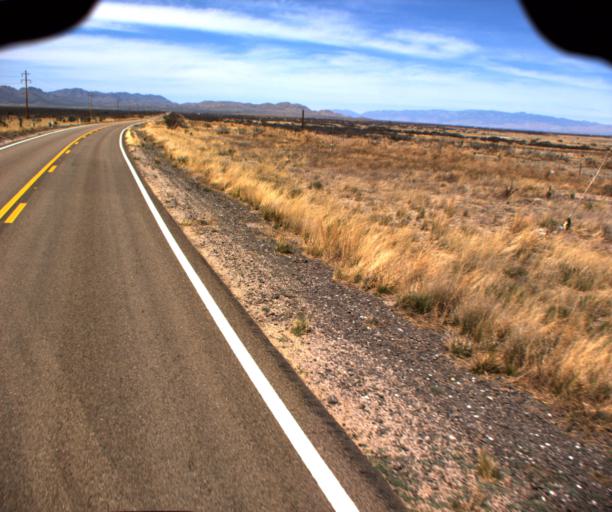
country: US
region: Arizona
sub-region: Cochise County
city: Willcox
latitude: 32.1451
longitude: -109.9334
